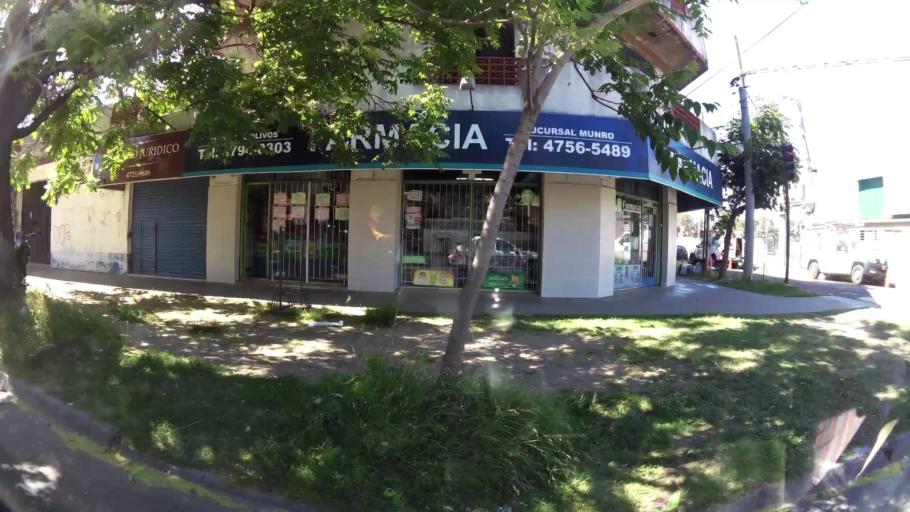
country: AR
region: Buenos Aires
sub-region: Partido de Vicente Lopez
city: Olivos
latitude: -34.5209
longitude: -58.5196
